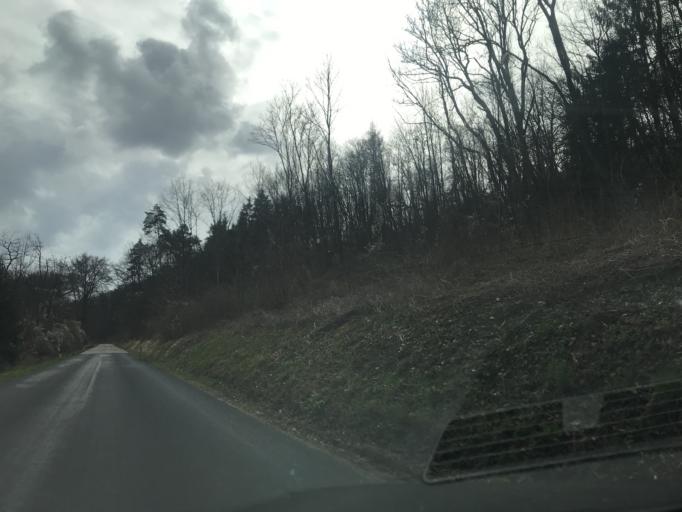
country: DE
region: Saarland
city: Blieskastel
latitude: 49.2029
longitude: 7.2362
